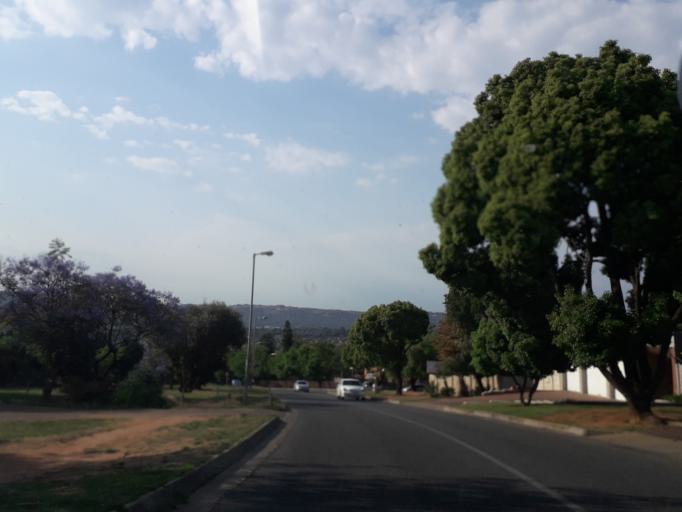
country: ZA
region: Gauteng
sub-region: City of Johannesburg Metropolitan Municipality
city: Roodepoort
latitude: -26.1085
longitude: 27.9403
